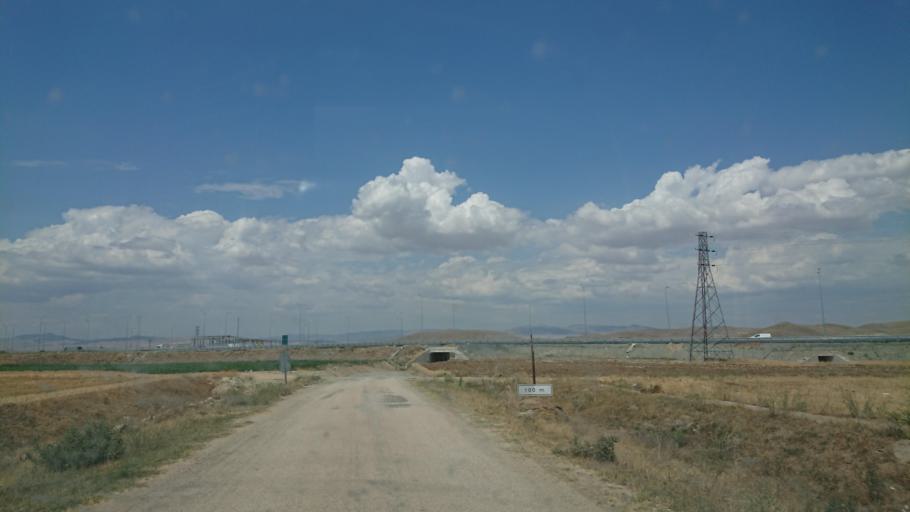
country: TR
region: Aksaray
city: Sariyahsi
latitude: 38.9727
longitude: 33.8989
